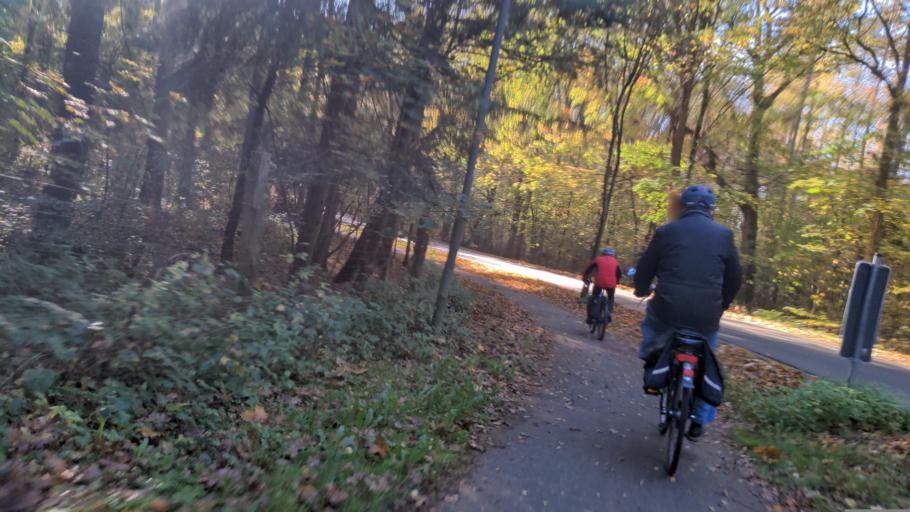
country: DE
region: Schleswig-Holstein
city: Ratekau
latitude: 53.9783
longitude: 10.7040
